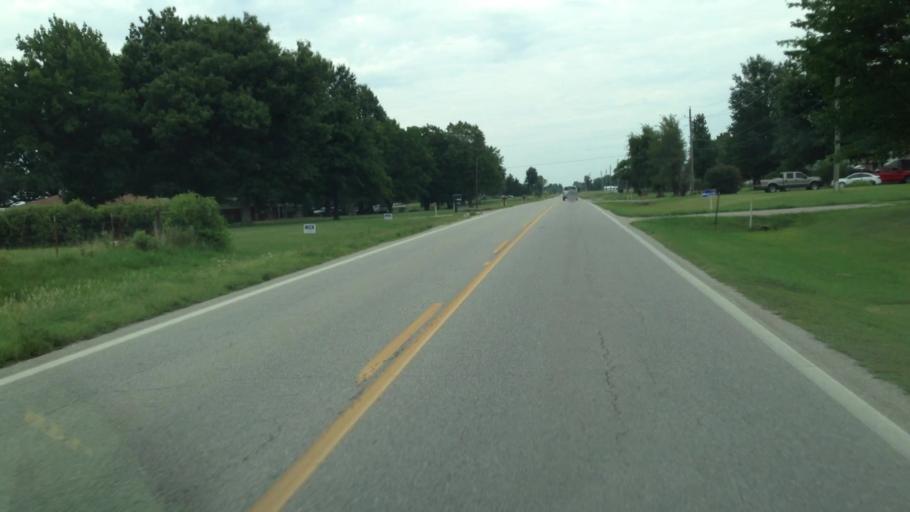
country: US
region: Oklahoma
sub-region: Craig County
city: Vinita
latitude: 36.6658
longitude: -95.1436
